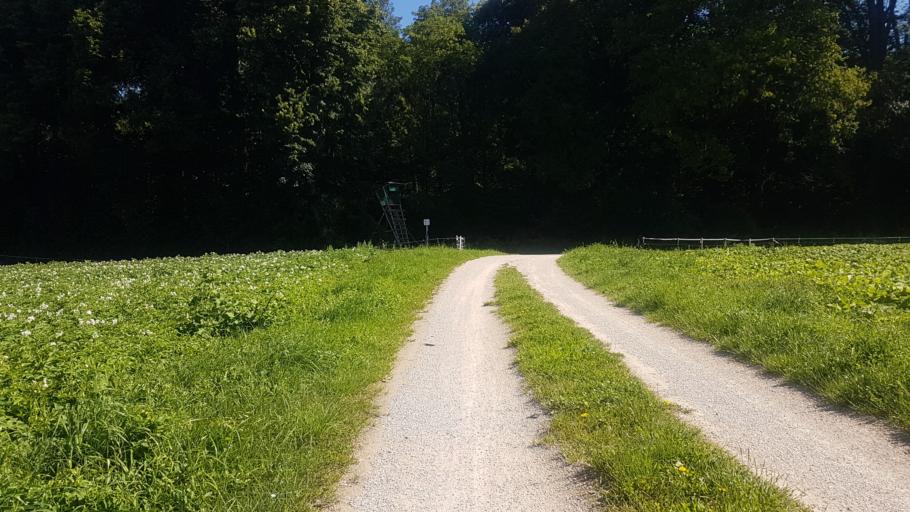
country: DE
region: Bavaria
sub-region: Upper Bavaria
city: Weichering
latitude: 48.7312
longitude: 11.2970
